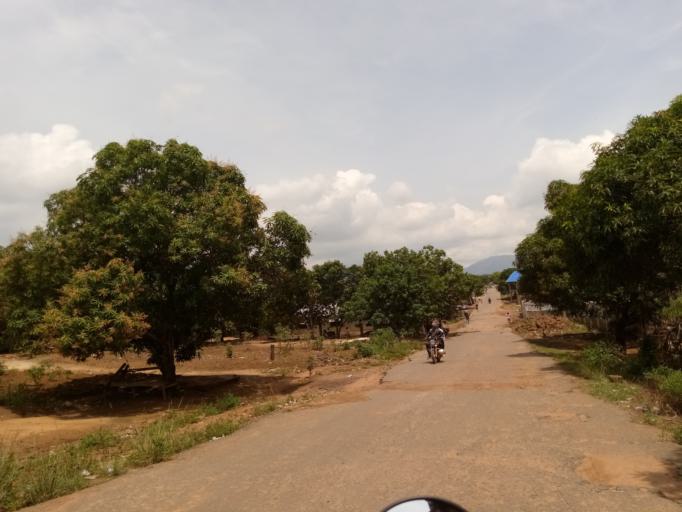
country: SL
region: Western Area
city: Waterloo
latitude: 8.3347
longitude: -13.0364
